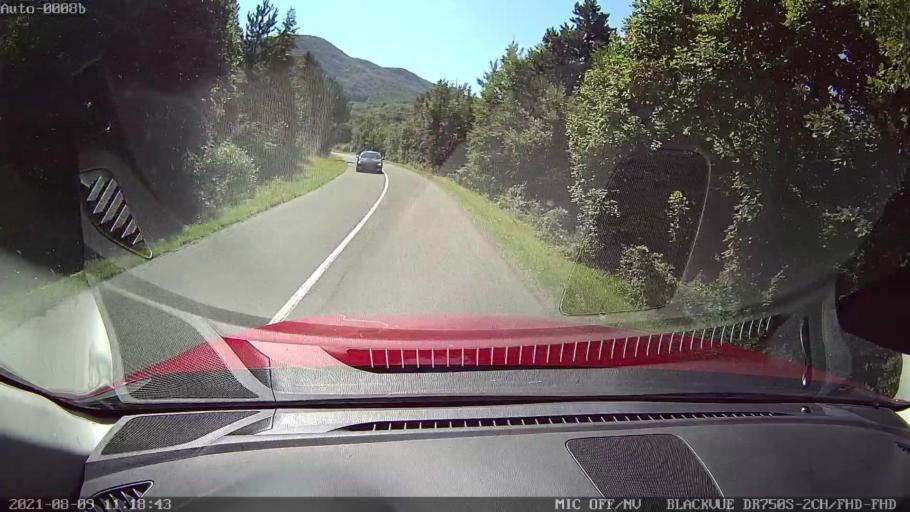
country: HR
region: Istarska
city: Lovran
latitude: 45.3085
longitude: 14.1924
